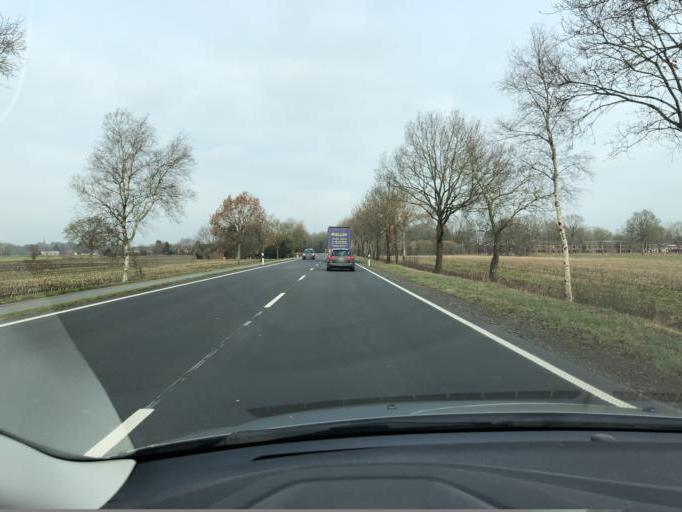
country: DE
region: Lower Saxony
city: Mittegrossefehn
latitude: 53.3849
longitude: 7.5797
